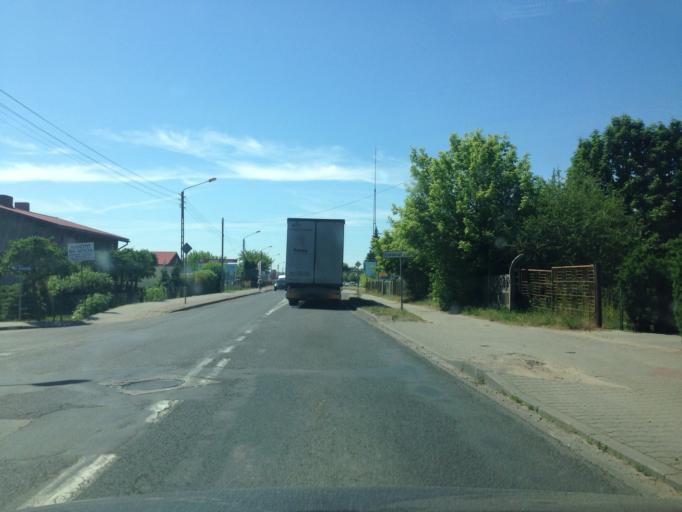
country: PL
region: Kujawsko-Pomorskie
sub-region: Powiat brodnicki
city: Brodnica
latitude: 53.2415
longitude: 19.3945
